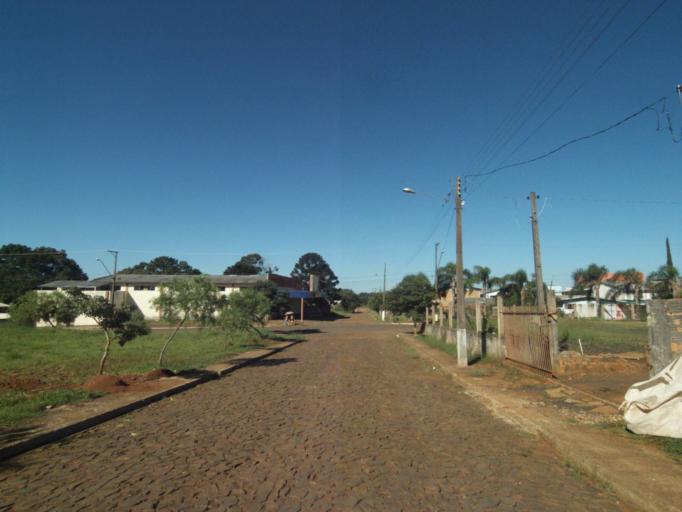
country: BR
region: Parana
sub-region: Pinhao
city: Pinhao
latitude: -25.8360
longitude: -52.0284
